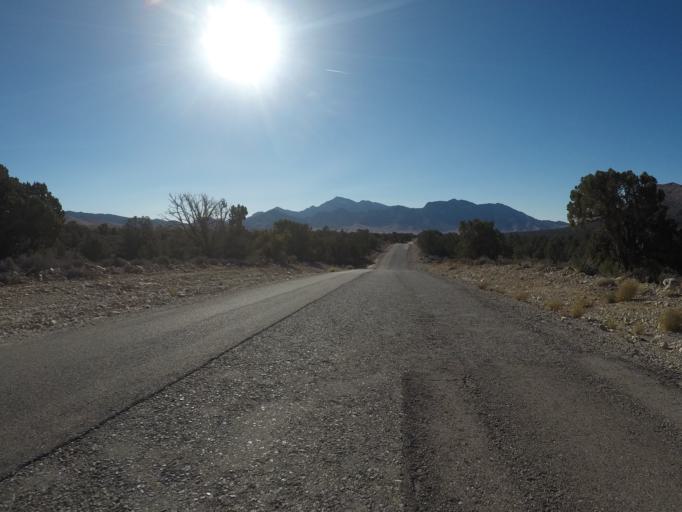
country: US
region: Nevada
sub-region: Clark County
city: Summerlin South
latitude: 36.0666
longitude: -115.5611
